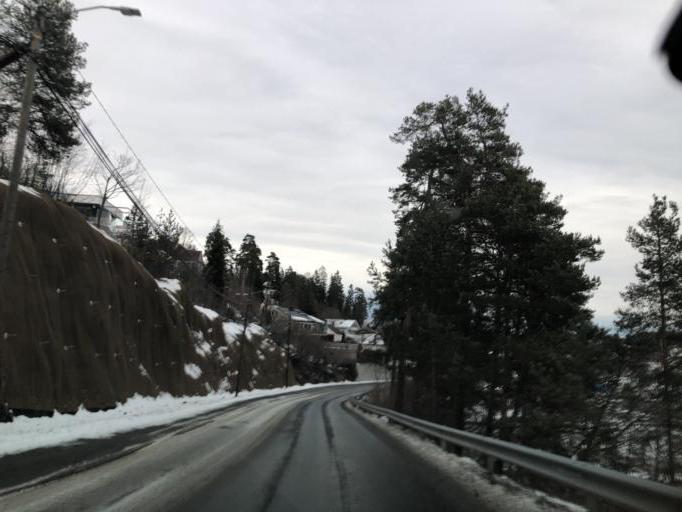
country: NO
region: Akershus
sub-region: Baerum
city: Sandvika
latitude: 59.8724
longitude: 10.5105
